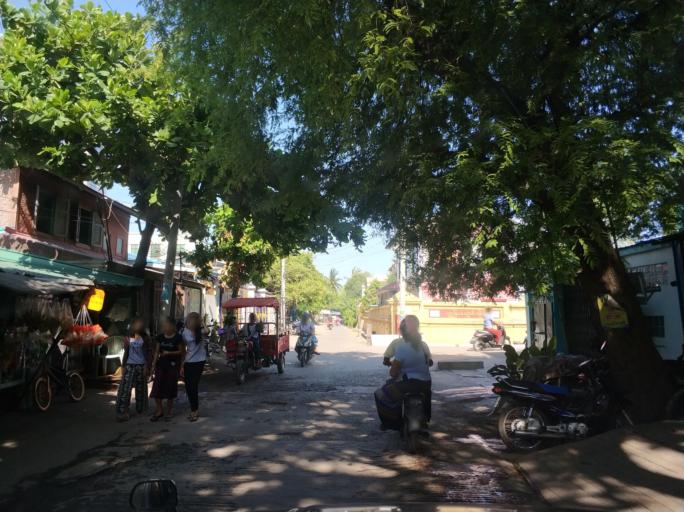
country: MM
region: Mandalay
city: Mandalay
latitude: 21.9718
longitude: 96.0702
